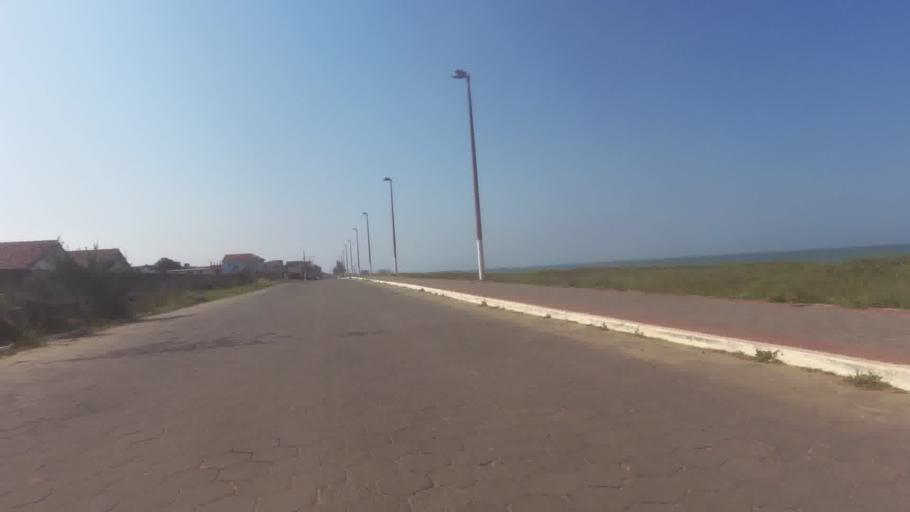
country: BR
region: Espirito Santo
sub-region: Itapemirim
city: Itapemirim
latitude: -21.0213
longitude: -40.8109
